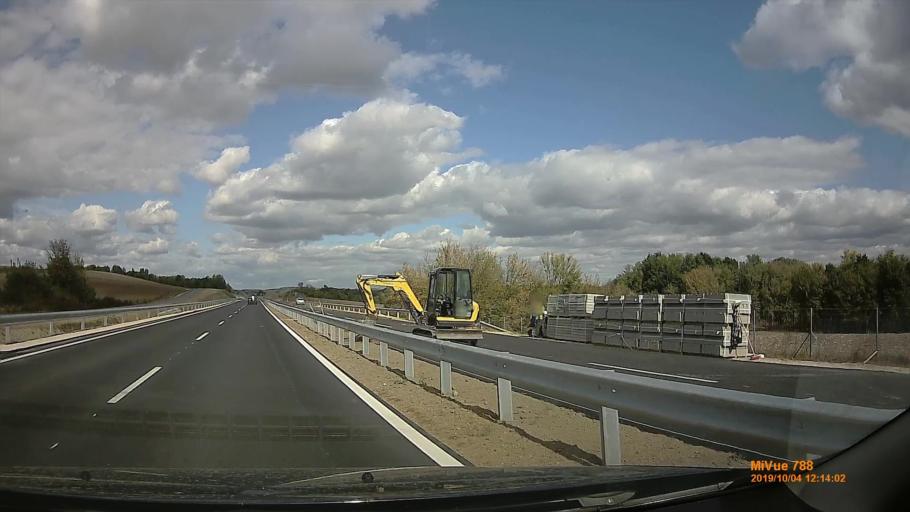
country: HU
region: Somogy
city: Karad
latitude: 46.5300
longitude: 17.8173
